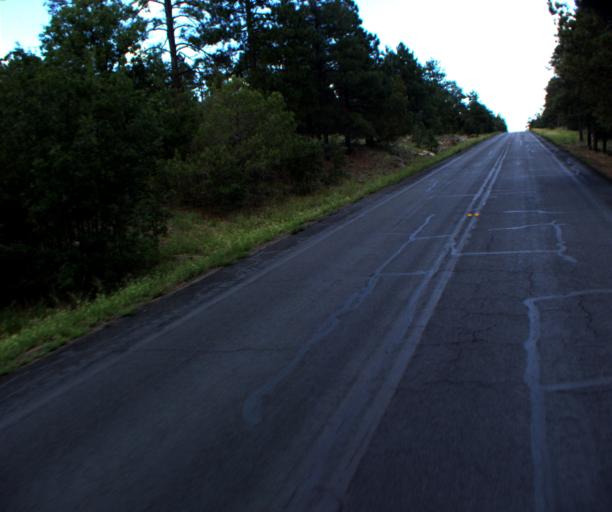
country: US
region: Arizona
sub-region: Gila County
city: Pine
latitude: 34.5070
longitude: -111.4733
